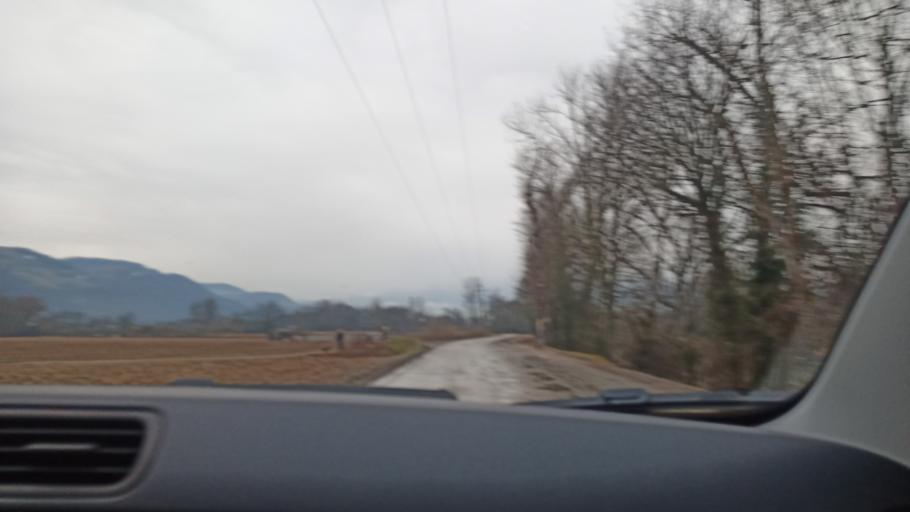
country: FR
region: Rhone-Alpes
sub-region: Departement de l'Isere
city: Domene
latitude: 45.2164
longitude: 5.8375
